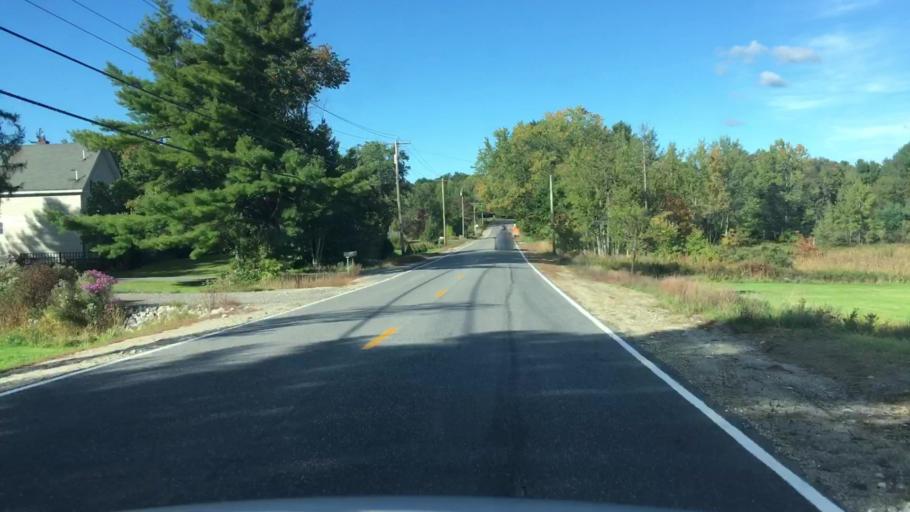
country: US
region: Maine
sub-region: Androscoggin County
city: Lisbon Falls
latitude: 43.9782
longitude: -70.0598
